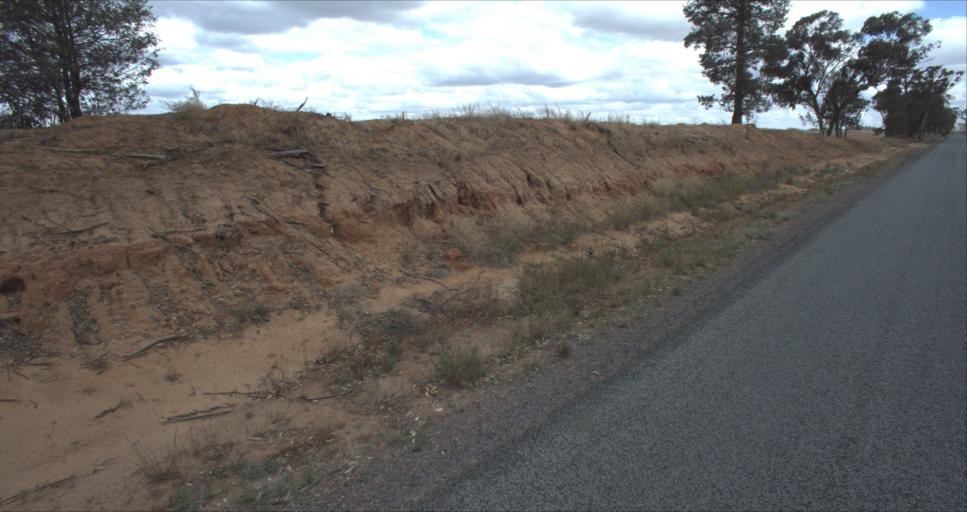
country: AU
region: New South Wales
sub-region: Leeton
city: Leeton
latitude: -34.6490
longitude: 146.3516
